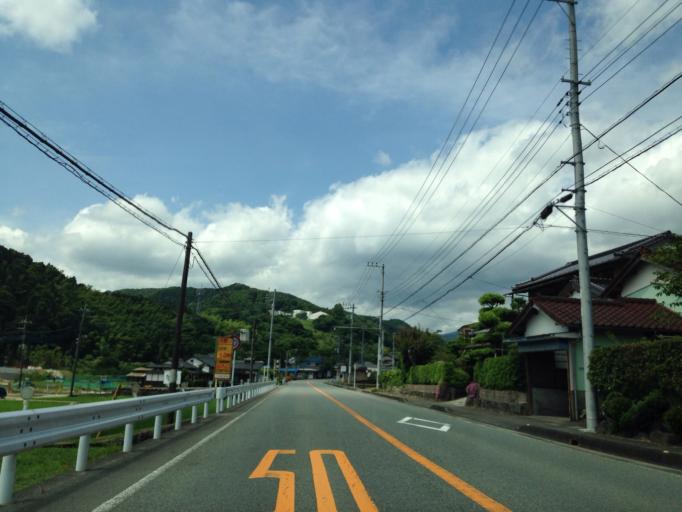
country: JP
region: Shizuoka
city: Heda
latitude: 34.9261
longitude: 138.9284
